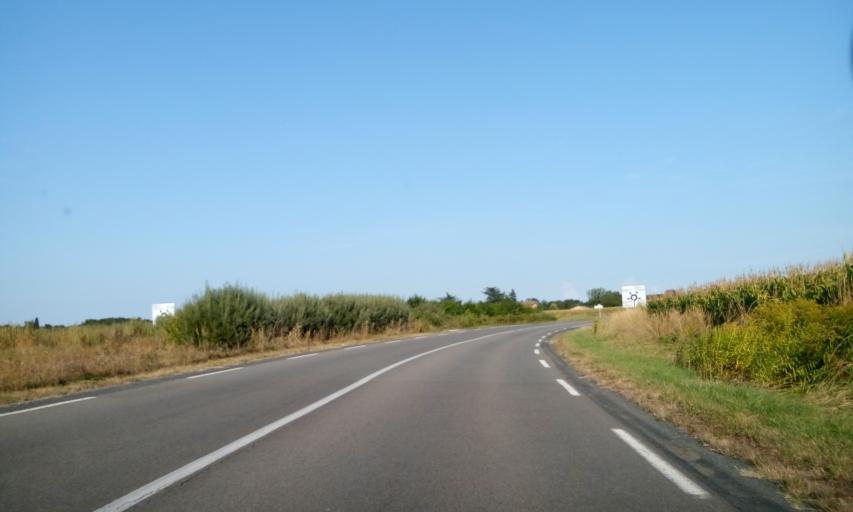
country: FR
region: Rhone-Alpes
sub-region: Departement de l'Ain
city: Sainte-Euphemie
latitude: 45.9851
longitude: 4.7930
